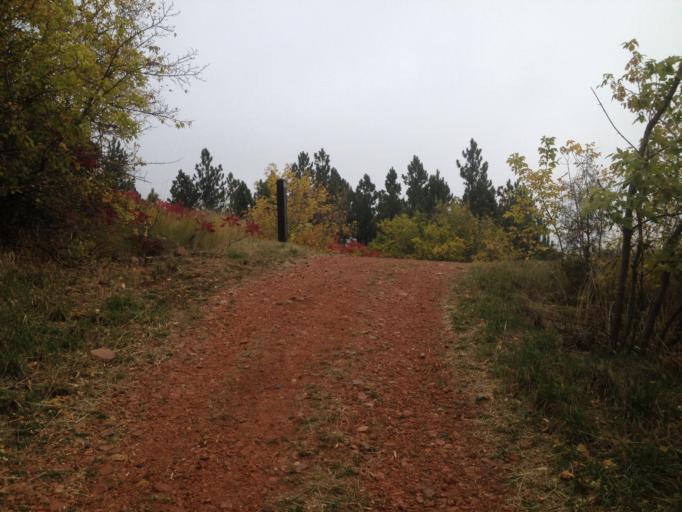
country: US
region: Colorado
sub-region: Boulder County
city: Boulder
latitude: 39.9247
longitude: -105.2784
